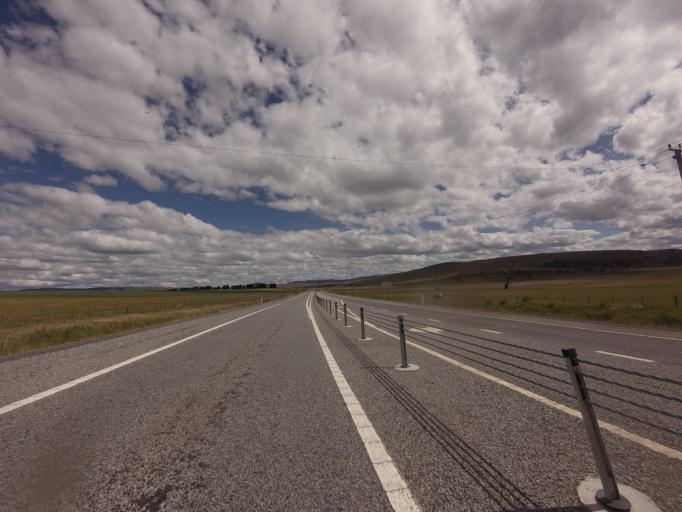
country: AU
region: Tasmania
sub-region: Northern Midlands
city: Evandale
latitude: -42.0958
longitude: 147.4543
